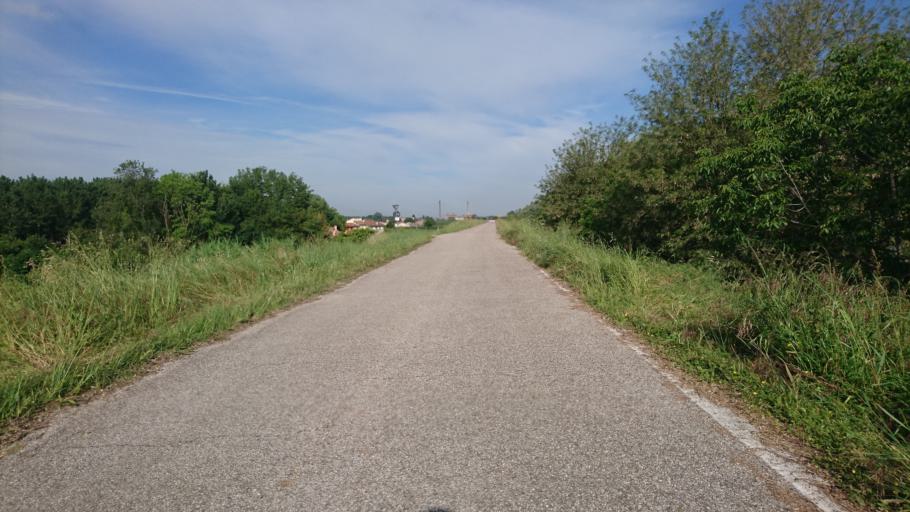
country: IT
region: Veneto
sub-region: Provincia di Rovigo
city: Castelnovo Bariano
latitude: 45.0160
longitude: 11.2751
